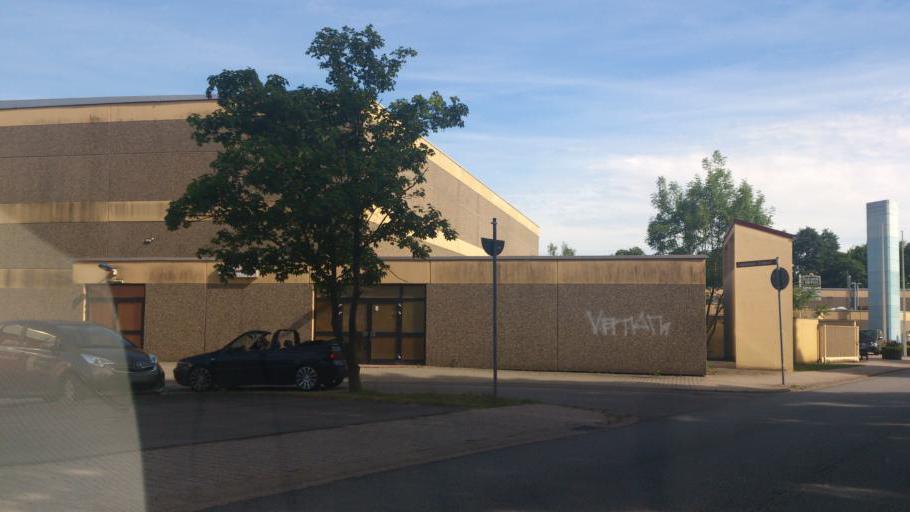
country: DE
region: Saarland
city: Bexbach
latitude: 49.3553
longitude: 7.2569
